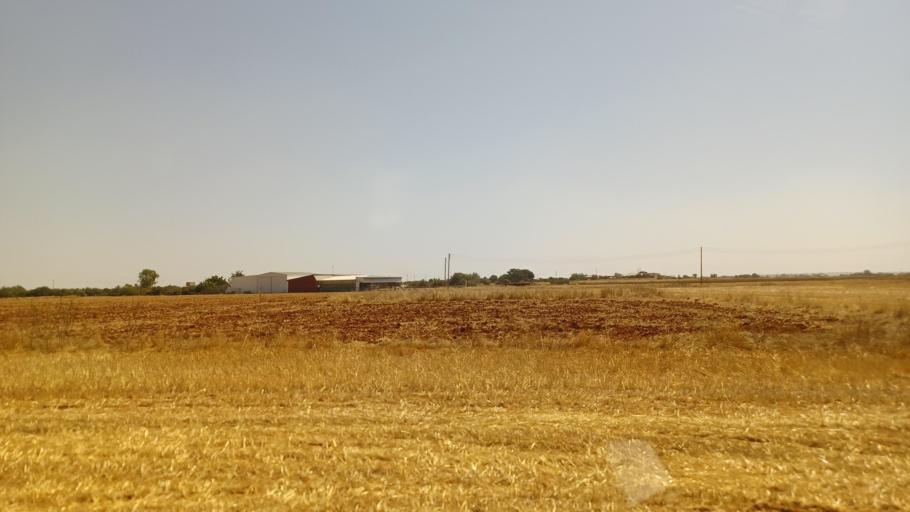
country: CY
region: Ammochostos
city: Avgorou
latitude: 35.0276
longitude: 33.8075
